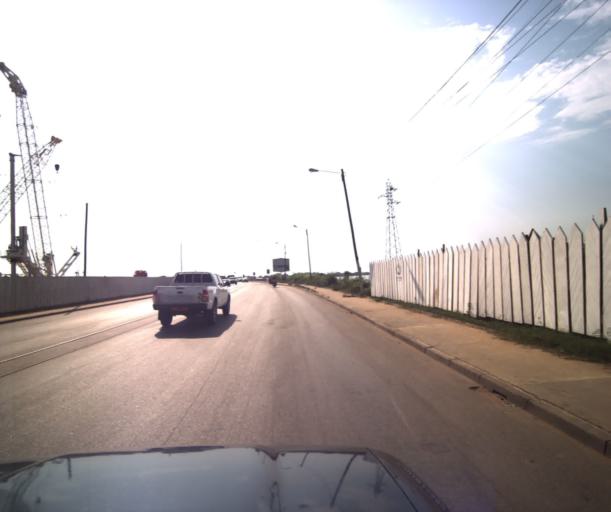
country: CM
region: Littoral
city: Bonaberi
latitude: 4.0725
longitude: 9.6972
